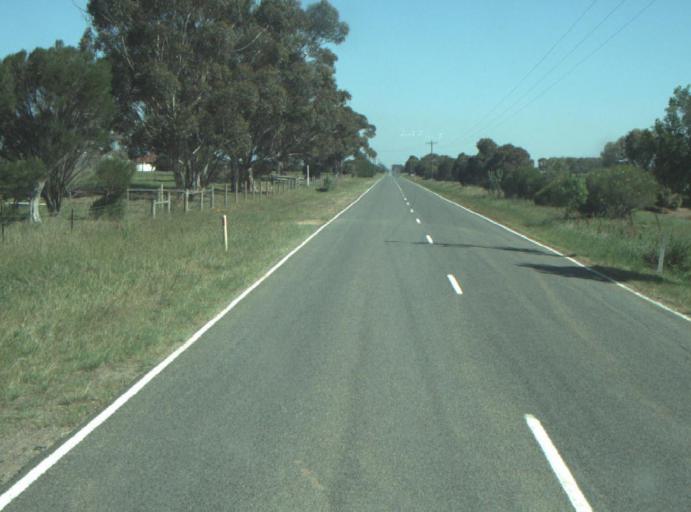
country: AU
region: Victoria
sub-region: Greater Geelong
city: Lara
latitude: -37.9755
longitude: 144.4048
